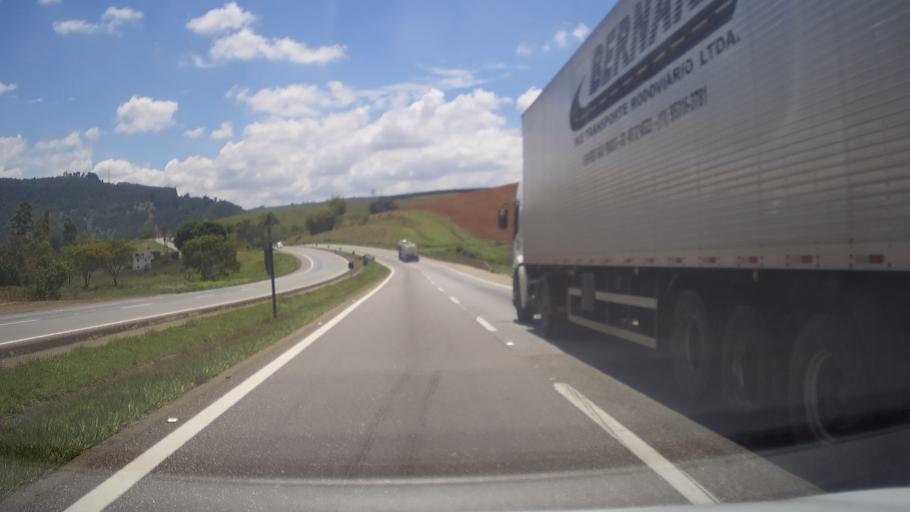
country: BR
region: Minas Gerais
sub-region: Campanha
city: Campanha
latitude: -21.8238
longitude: -45.4949
